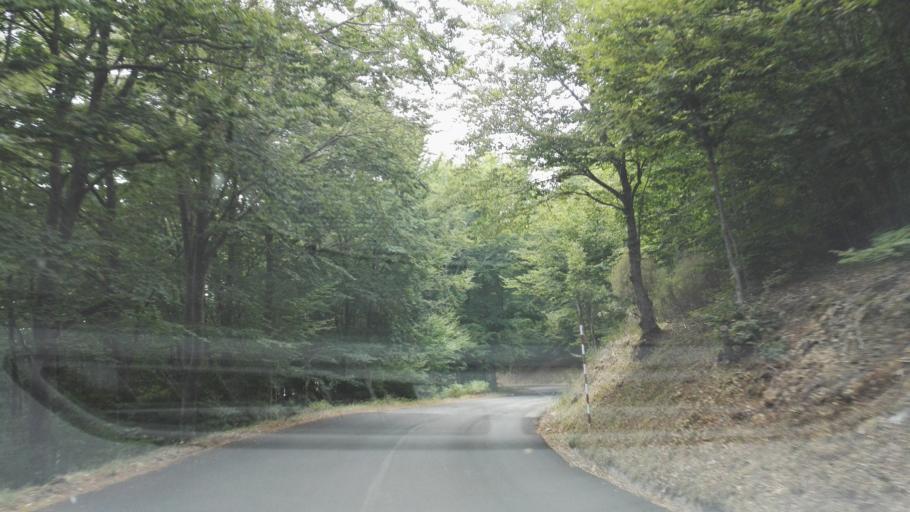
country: IT
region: Calabria
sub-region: Provincia di Vibo-Valentia
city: Nardodipace
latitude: 38.4913
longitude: 16.3473
